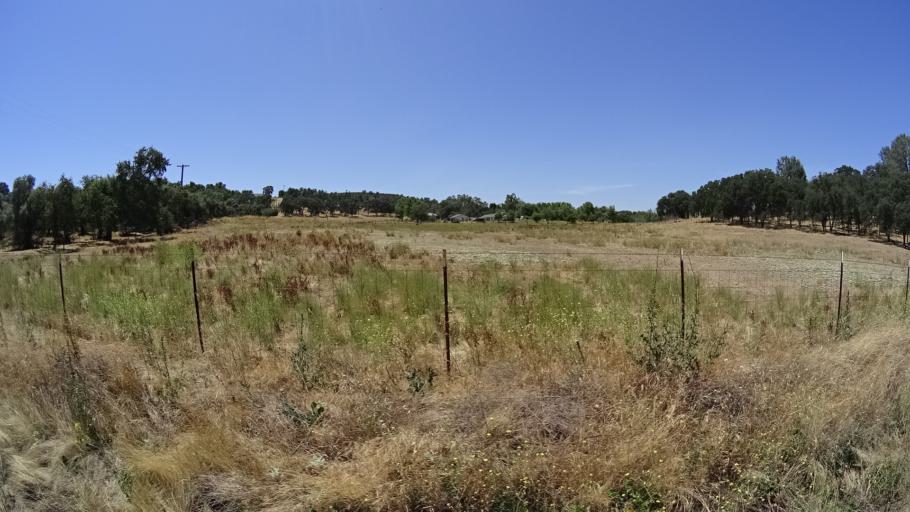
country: US
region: California
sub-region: Calaveras County
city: Rancho Calaveras
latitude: 38.1398
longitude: -120.8907
